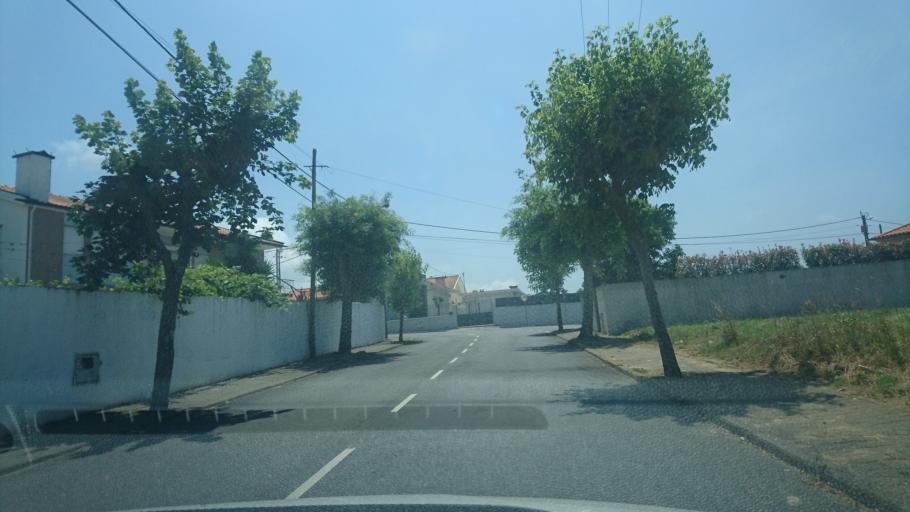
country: PT
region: Aveiro
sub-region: Ovar
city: Esmoriz
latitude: 40.9530
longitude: -8.6279
